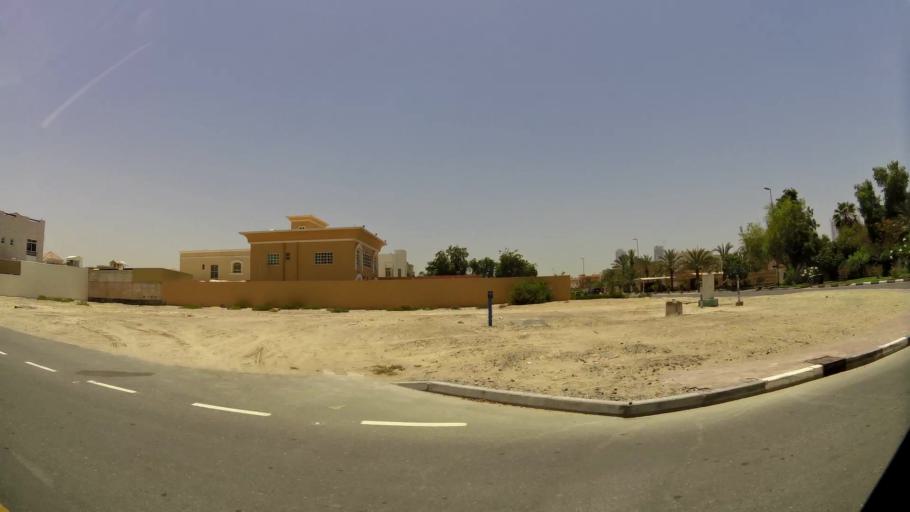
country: AE
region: Dubai
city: Dubai
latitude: 25.1028
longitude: 55.1987
